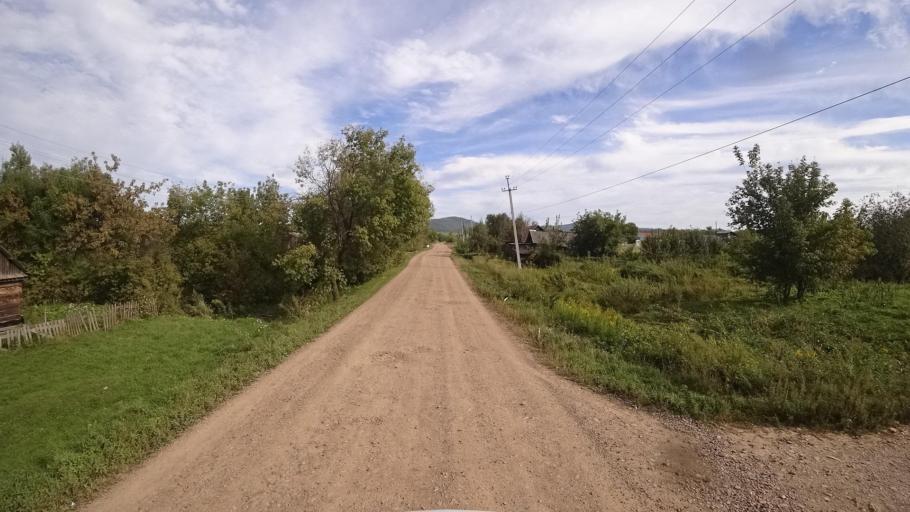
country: RU
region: Primorskiy
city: Dostoyevka
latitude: 44.3071
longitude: 133.4564
